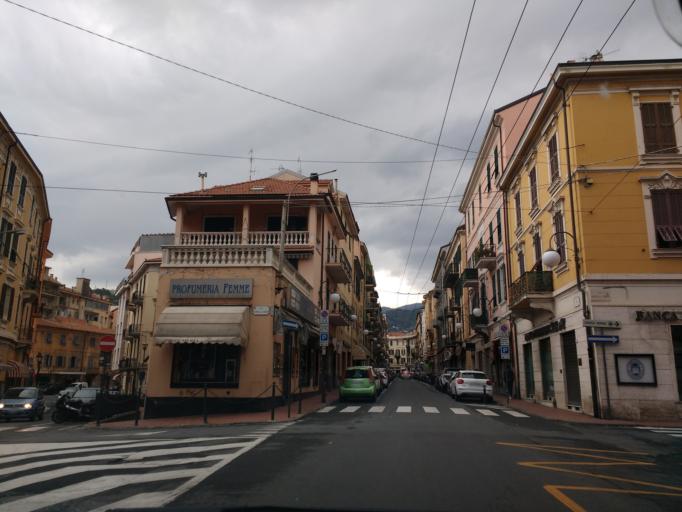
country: IT
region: Liguria
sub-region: Provincia di Imperia
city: Ventimiglia
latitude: 43.7920
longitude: 7.6084
